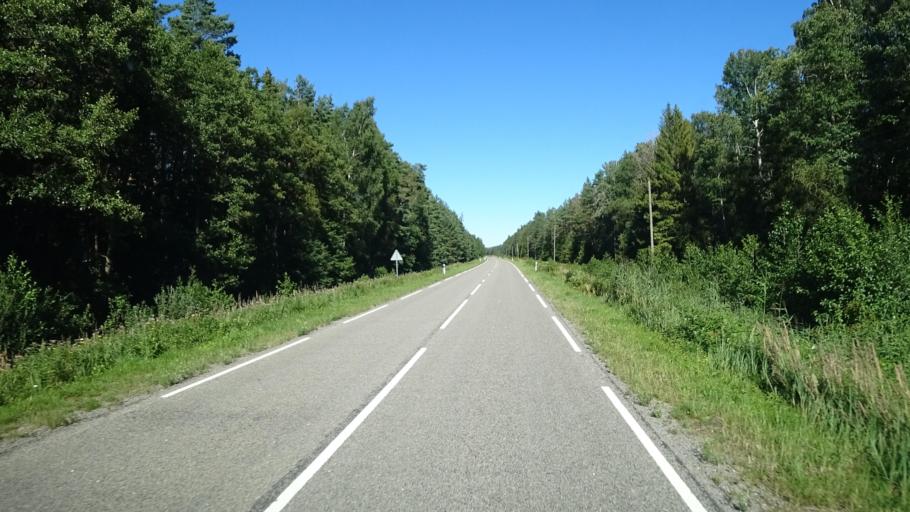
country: LV
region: Dundaga
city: Dundaga
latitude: 57.6872
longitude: 22.3719
